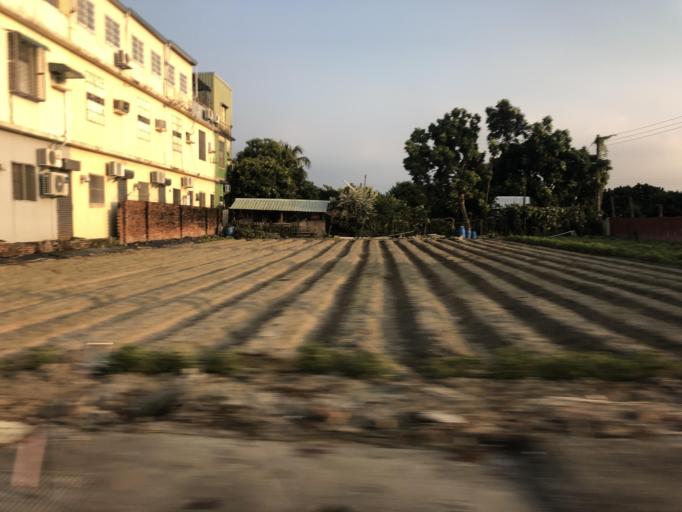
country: TW
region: Taiwan
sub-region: Tainan
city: Tainan
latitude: 23.1334
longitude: 120.2578
